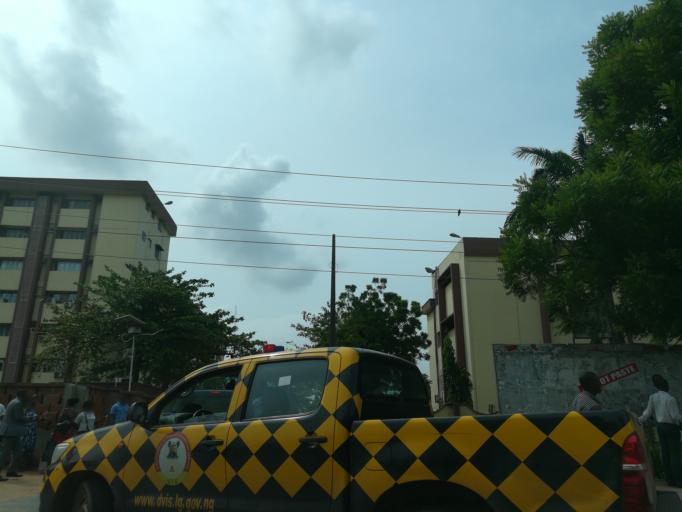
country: NG
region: Lagos
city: Ikeja
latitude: 6.6171
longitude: 3.3596
